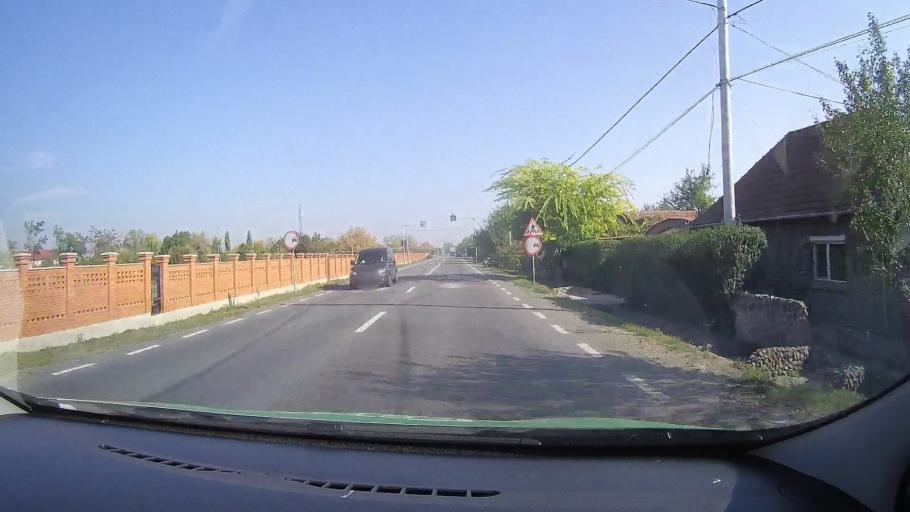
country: RO
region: Bihor
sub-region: Municipiul Salonta
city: Salonta
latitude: 46.7964
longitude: 21.6413
